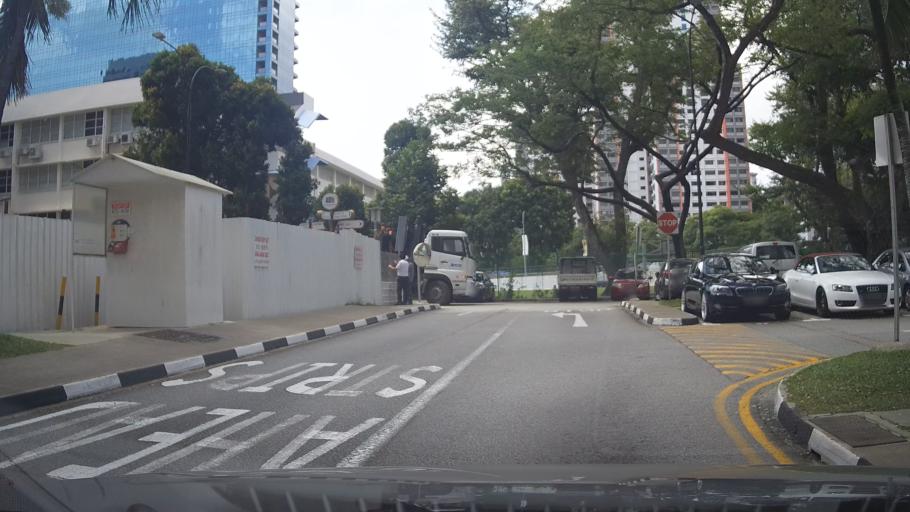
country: SG
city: Singapore
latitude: 1.3052
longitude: 103.8624
